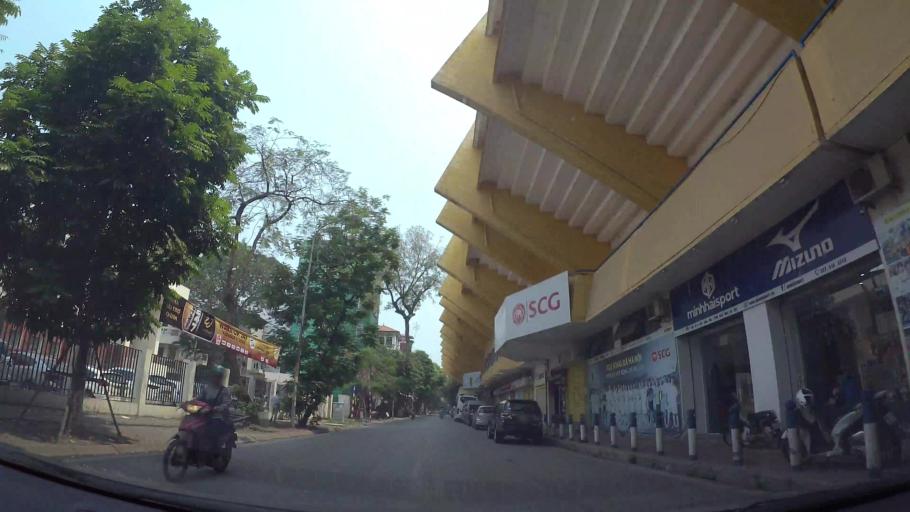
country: VN
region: Ha Noi
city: Dong Da
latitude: 21.0296
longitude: 105.8320
